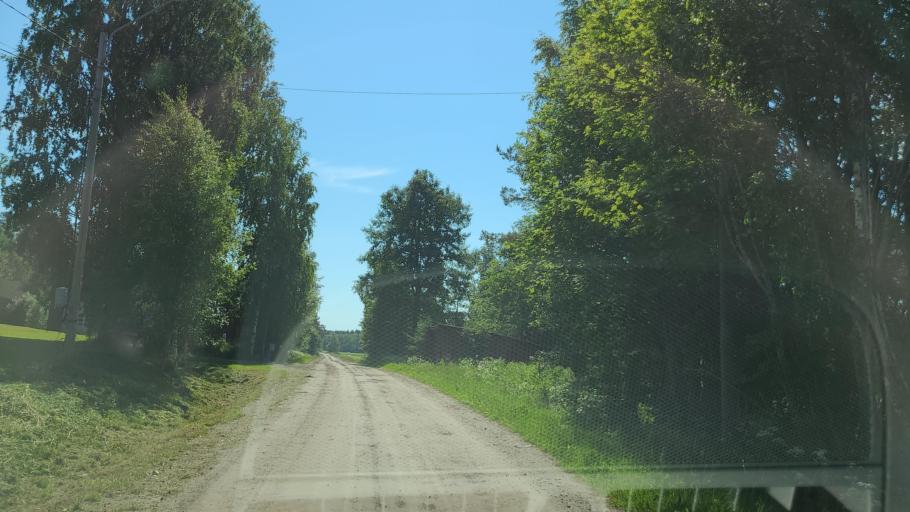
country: SE
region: Vaesterbotten
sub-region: Robertsfors Kommun
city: Robertsfors
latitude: 64.0852
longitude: 20.8427
